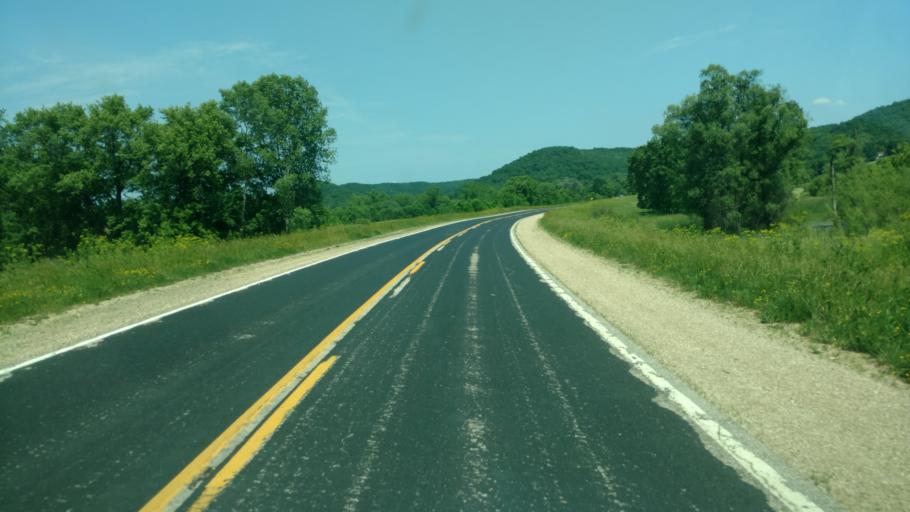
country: US
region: Wisconsin
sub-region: Vernon County
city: Westby
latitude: 43.5559
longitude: -90.6578
